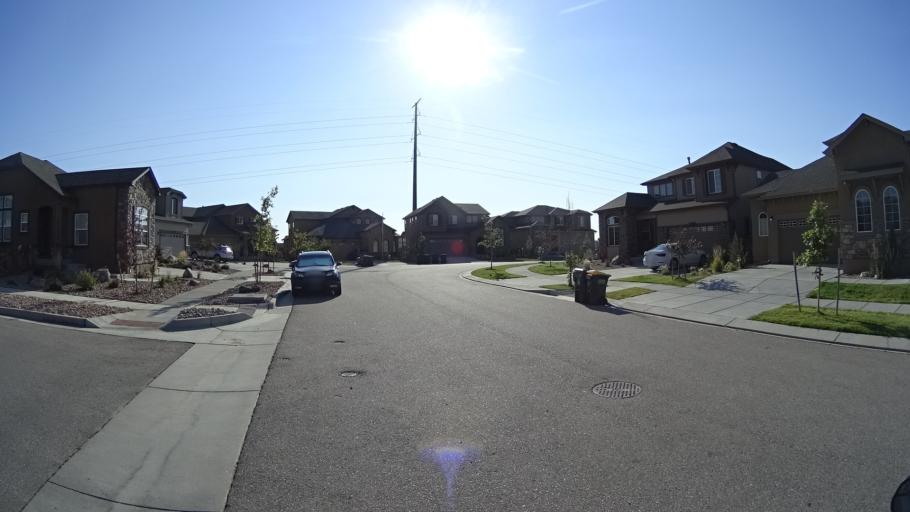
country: US
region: Colorado
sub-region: El Paso County
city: Cimarron Hills
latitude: 38.9353
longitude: -104.6648
